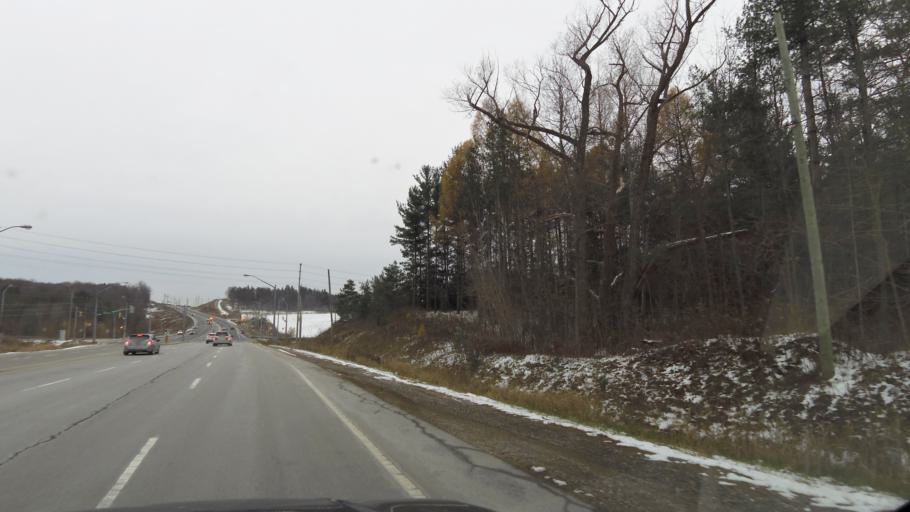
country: CA
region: Ontario
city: Newmarket
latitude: 44.0685
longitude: -79.5112
